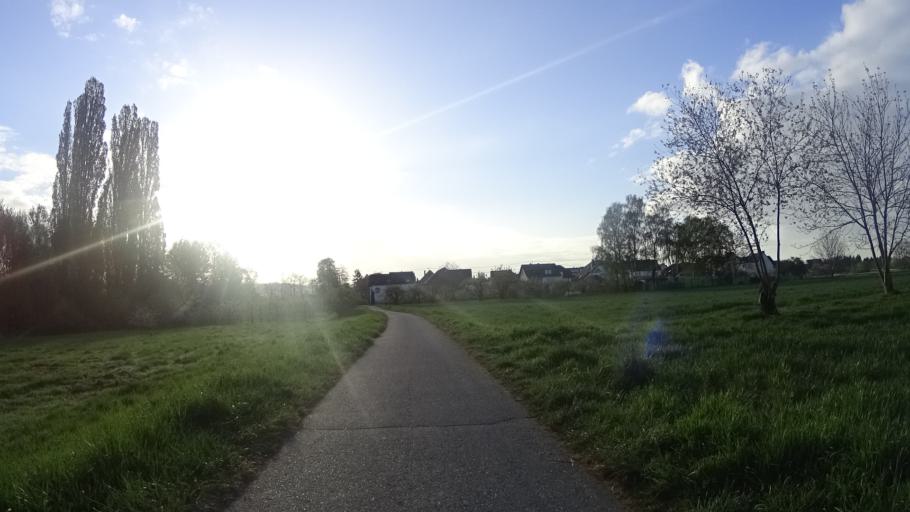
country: DE
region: Rheinland-Pfalz
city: Kaltenengers
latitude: 50.4189
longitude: 7.5370
